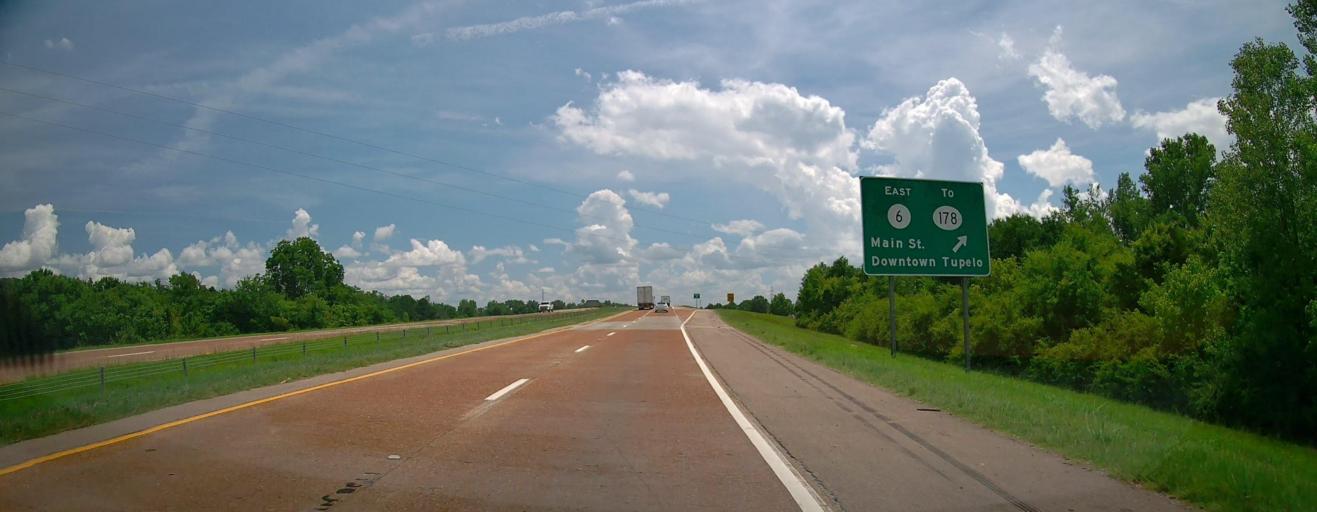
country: US
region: Mississippi
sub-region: Lee County
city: Tupelo
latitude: 34.2644
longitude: -88.6940
